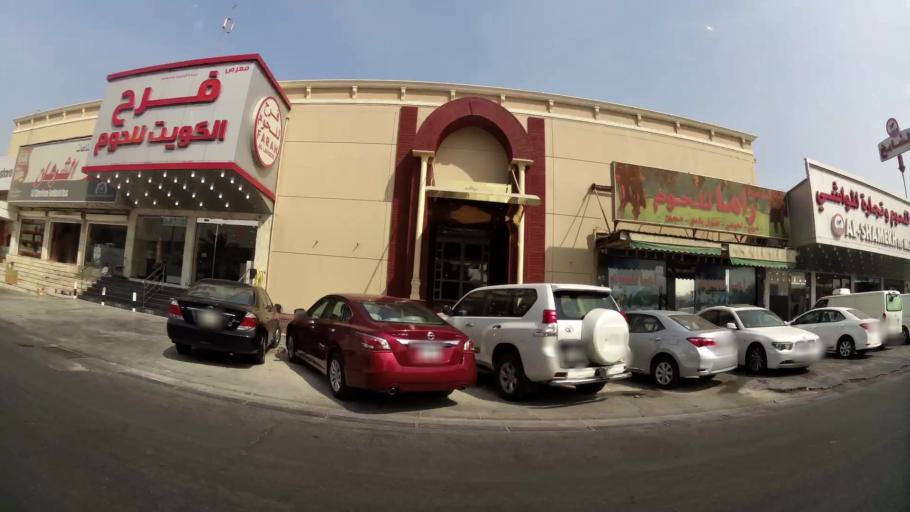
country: KW
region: Al Asimah
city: Ar Rabiyah
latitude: 29.3239
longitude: 47.9293
